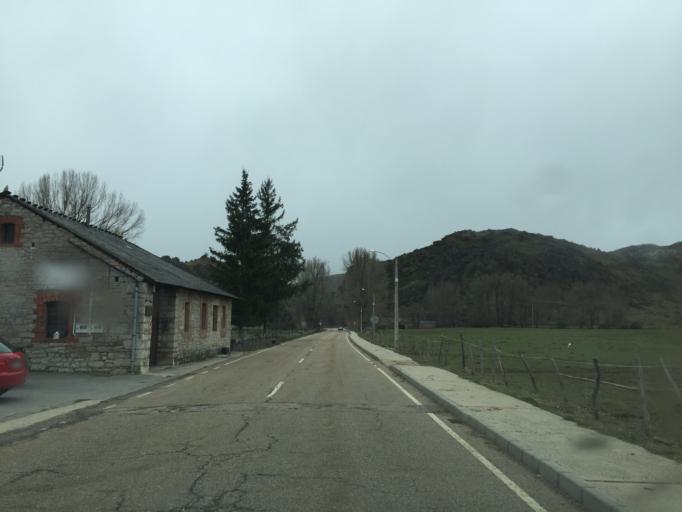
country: ES
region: Castille and Leon
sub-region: Provincia de Leon
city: San Emiliano
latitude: 42.9691
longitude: -6.0020
